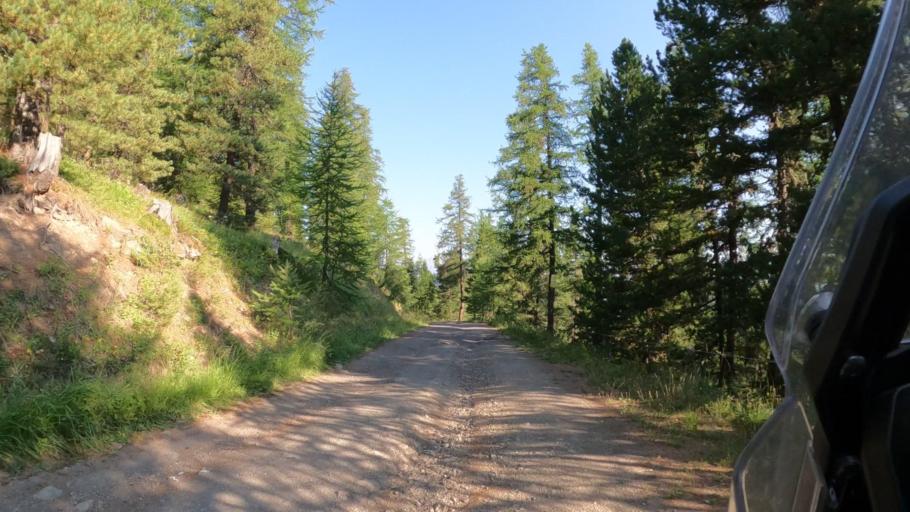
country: FR
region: Provence-Alpes-Cote d'Azur
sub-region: Departement des Hautes-Alpes
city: Guillestre
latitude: 44.6165
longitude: 6.6469
